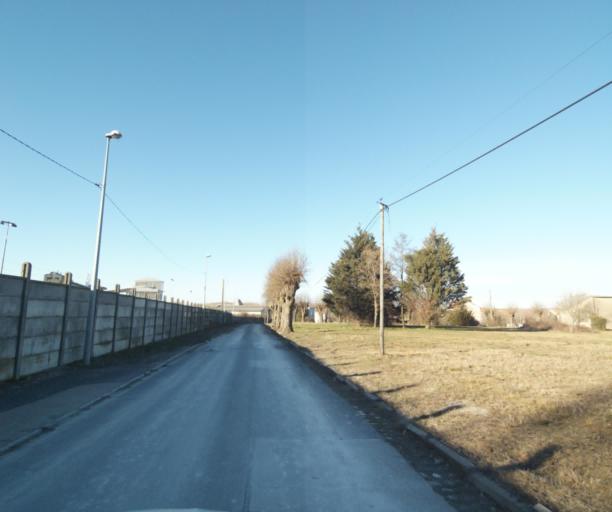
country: FR
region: Lorraine
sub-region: Departement de Meurthe-et-Moselle
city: Art-sur-Meurthe
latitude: 48.6380
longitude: 6.2686
